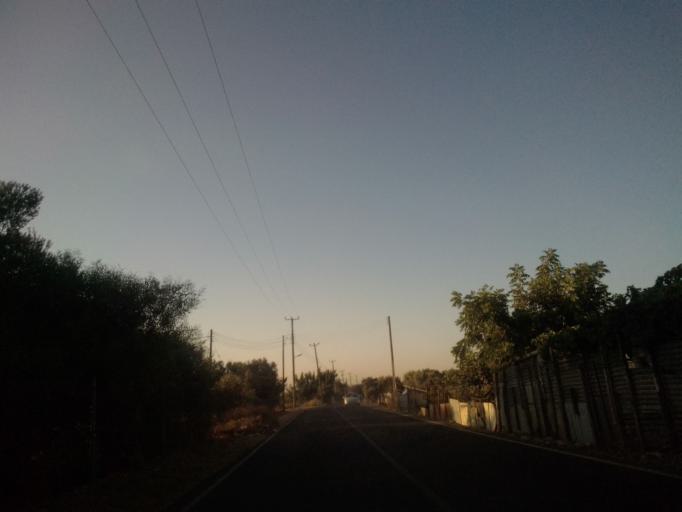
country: CY
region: Limassol
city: Ypsonas
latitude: 34.6786
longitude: 32.9562
